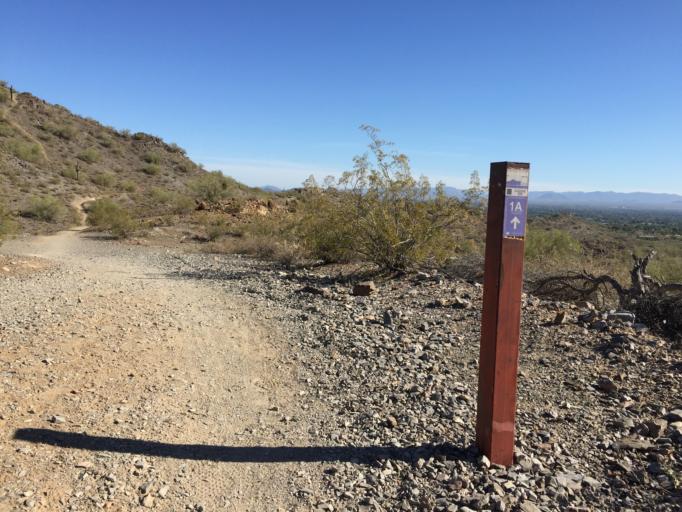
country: US
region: Arizona
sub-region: Maricopa County
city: Paradise Valley
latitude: 33.5580
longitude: -112.0203
